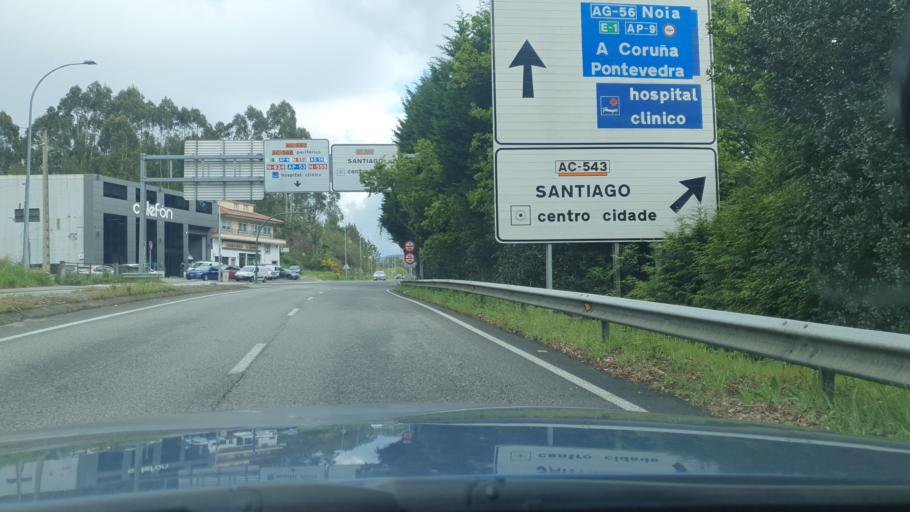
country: ES
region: Galicia
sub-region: Provincia da Coruna
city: Santiago de Compostela
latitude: 42.8721
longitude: -8.5797
